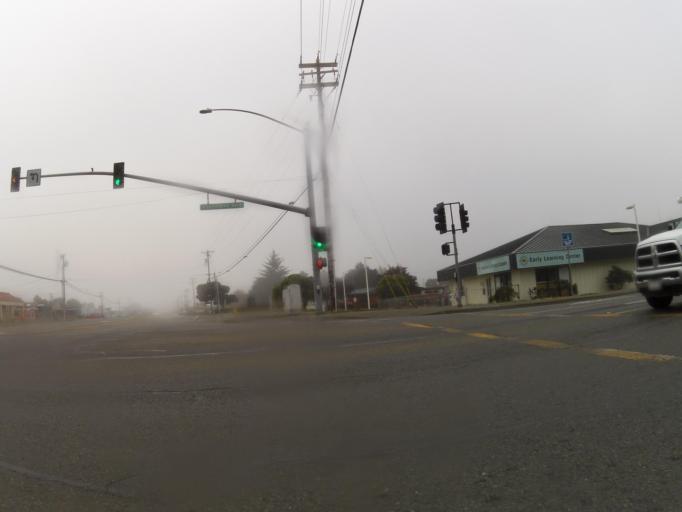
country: US
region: California
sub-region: Del Norte County
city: Crescent City
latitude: 41.7727
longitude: -124.2002
